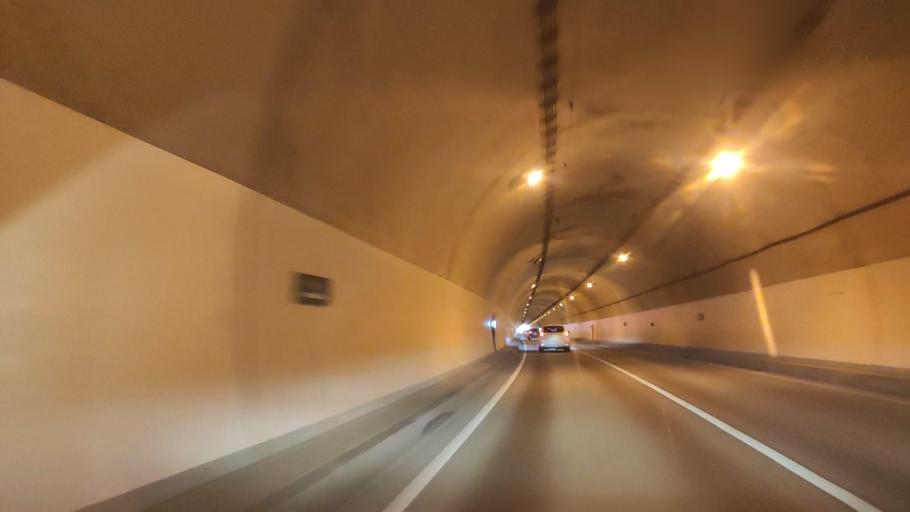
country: JP
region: Hokkaido
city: Ishikari
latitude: 43.4767
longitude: 141.3951
